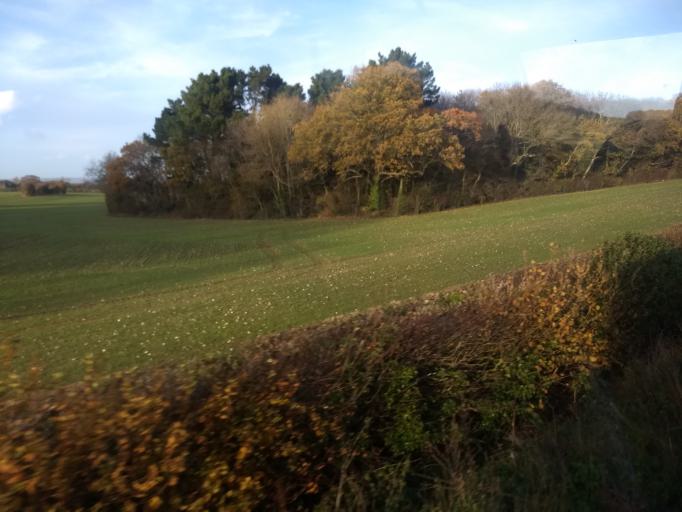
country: GB
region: England
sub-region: Isle of Wight
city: Shalfleet
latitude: 50.6810
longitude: -1.3950
